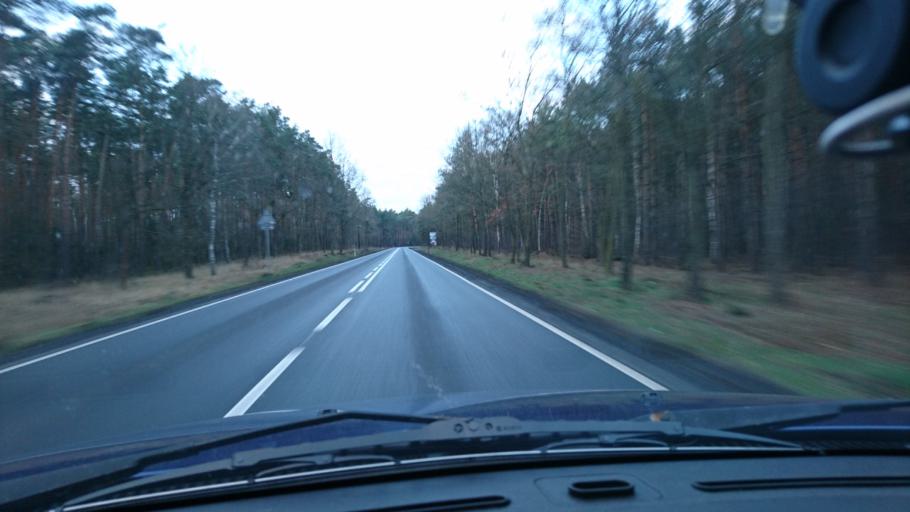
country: PL
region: Greater Poland Voivodeship
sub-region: Powiat kepinski
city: Kepno
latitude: 51.3353
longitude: 17.9554
